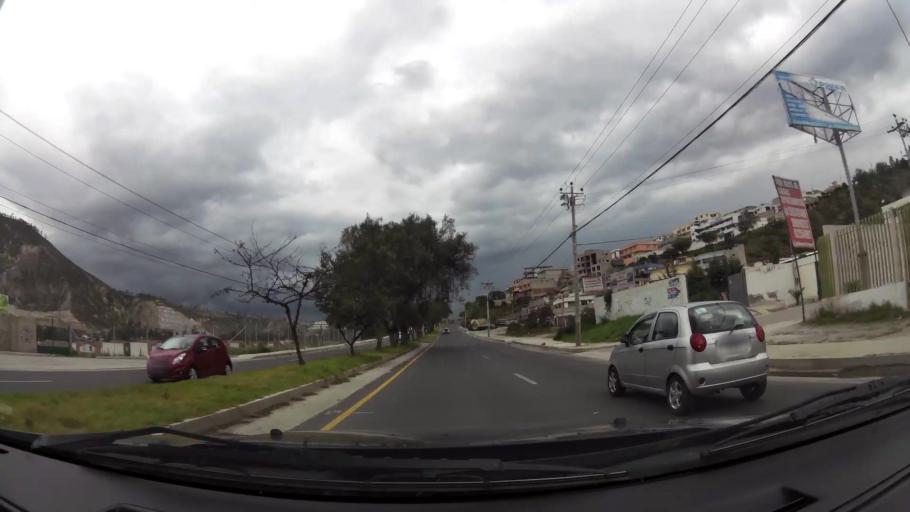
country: EC
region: Pichincha
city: Quito
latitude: -0.0458
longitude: -78.4553
